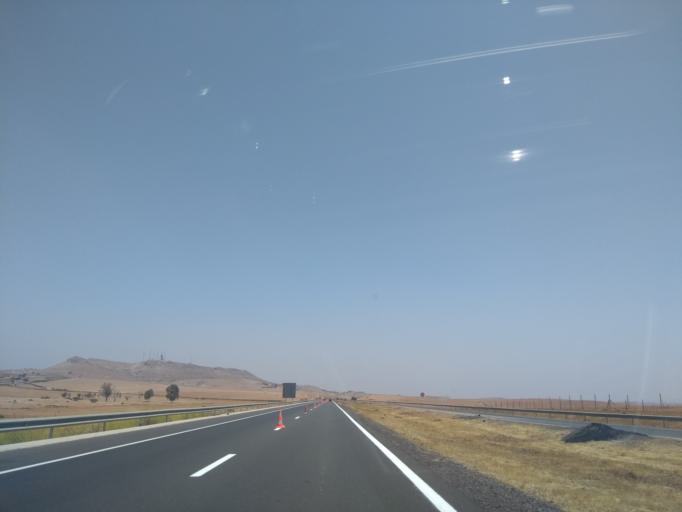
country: MA
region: Marrakech-Tensift-Al Haouz
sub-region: Kelaa-Des-Sraghna
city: Sidi Abdallah
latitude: 32.4488
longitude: -7.9315
